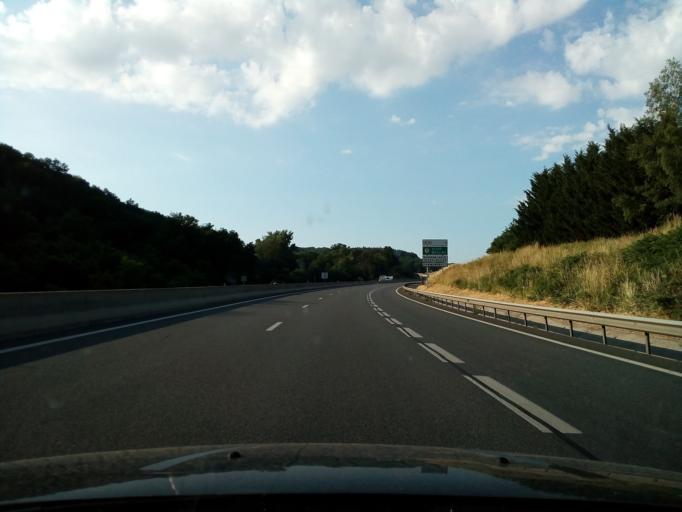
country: FR
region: Auvergne
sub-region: Departement de l'Allier
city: Desertines
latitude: 46.3762
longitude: 2.6289
